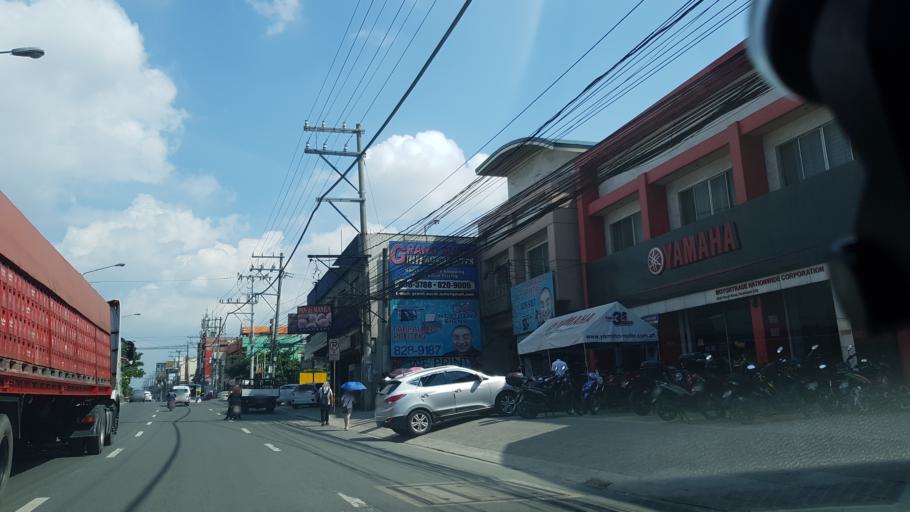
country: PH
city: Sambayanihan People's Village
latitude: 14.4747
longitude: 121.0016
